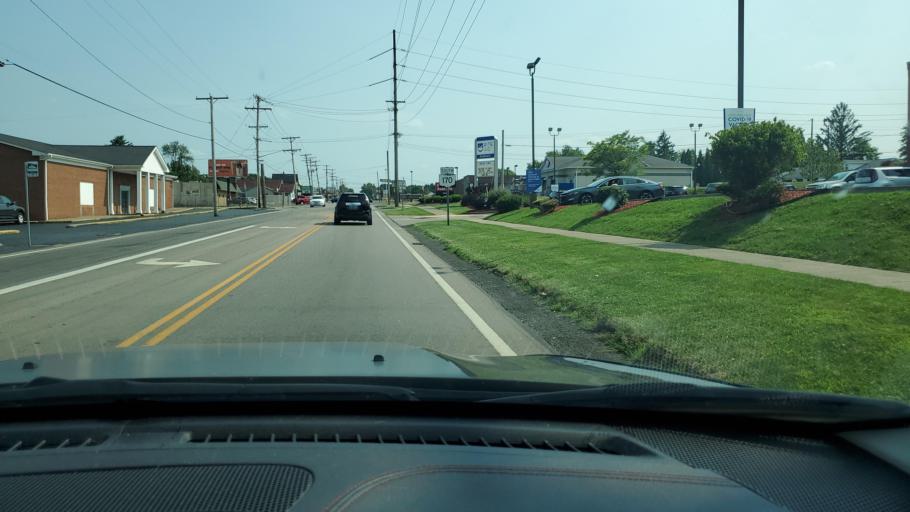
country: US
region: Ohio
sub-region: Mahoning County
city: Struthers
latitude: 41.0508
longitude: -80.6158
